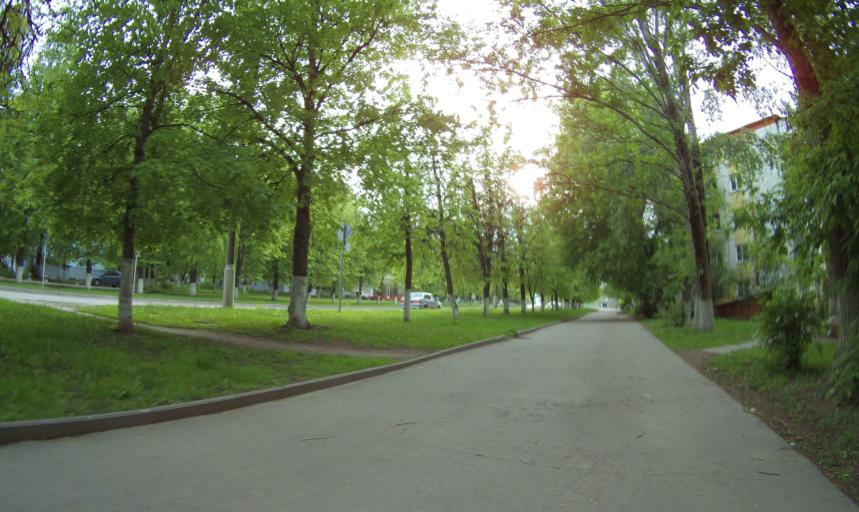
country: RU
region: Moskovskaya
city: Kolomna
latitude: 55.0870
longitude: 38.7697
